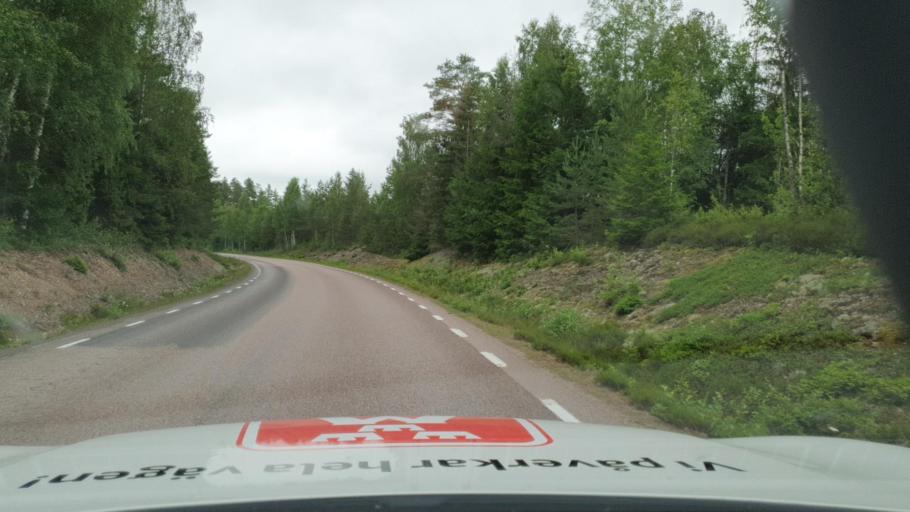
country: SE
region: Vaermland
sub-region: Kristinehamns Kommun
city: Kristinehamn
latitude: 59.4747
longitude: 13.9387
